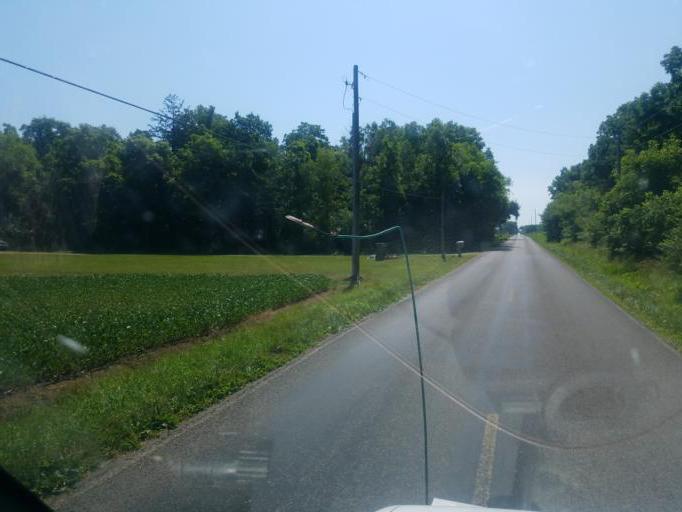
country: US
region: Ohio
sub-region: Champaign County
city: North Lewisburg
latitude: 40.2172
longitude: -83.5108
